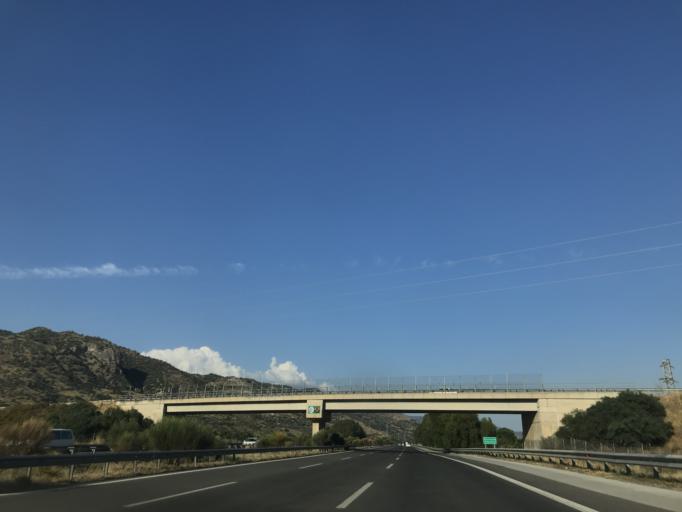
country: TR
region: Aydin
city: Incirliova
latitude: 37.8683
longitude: 27.7280
